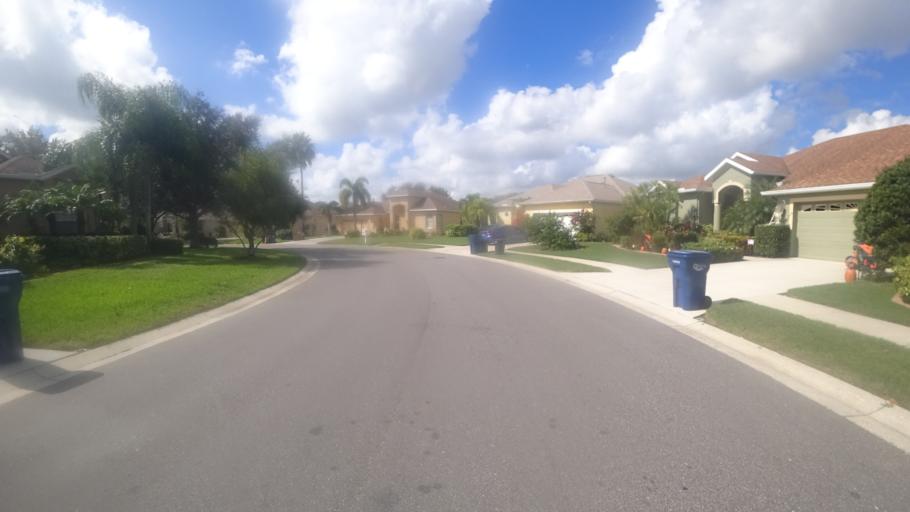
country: US
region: Florida
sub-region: Manatee County
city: Ellenton
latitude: 27.4963
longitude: -82.4419
